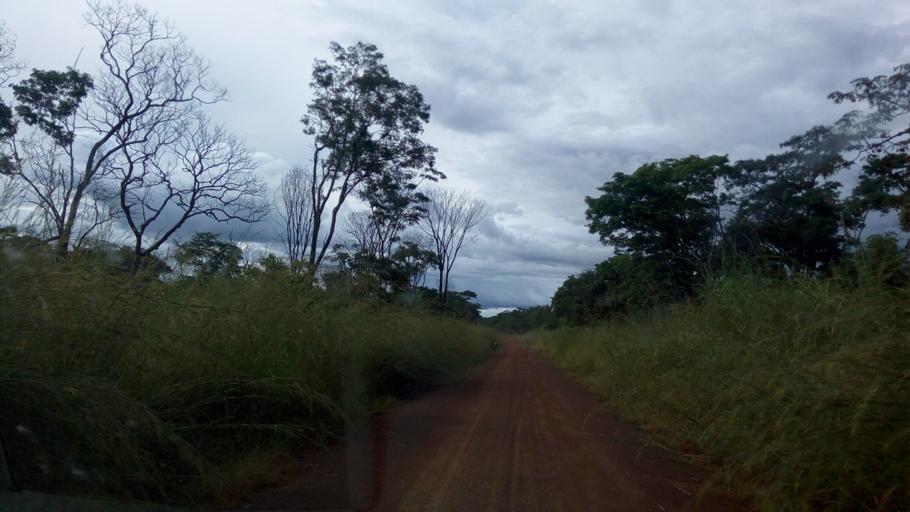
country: ZM
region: Luapula
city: Mwense
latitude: -10.3311
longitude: 28.1111
